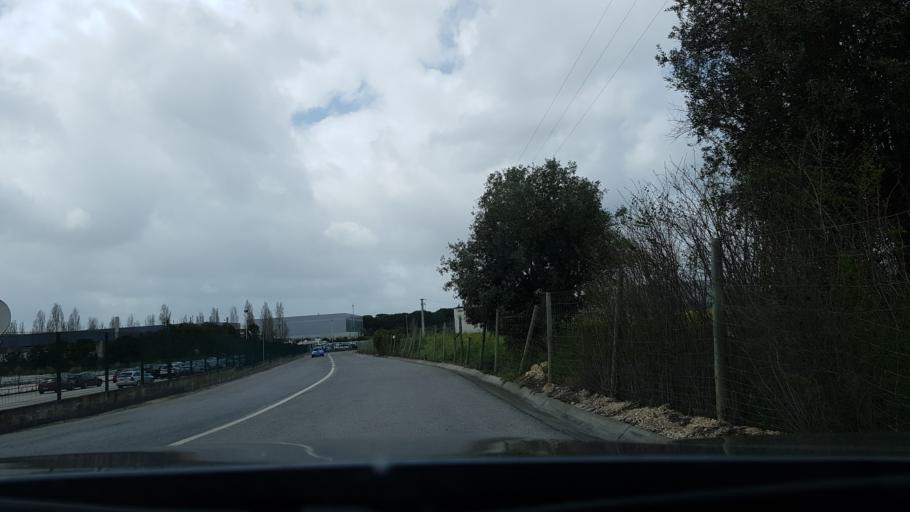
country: PT
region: Lisbon
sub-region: Alenquer
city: Carregado
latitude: 39.0330
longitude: -8.9704
